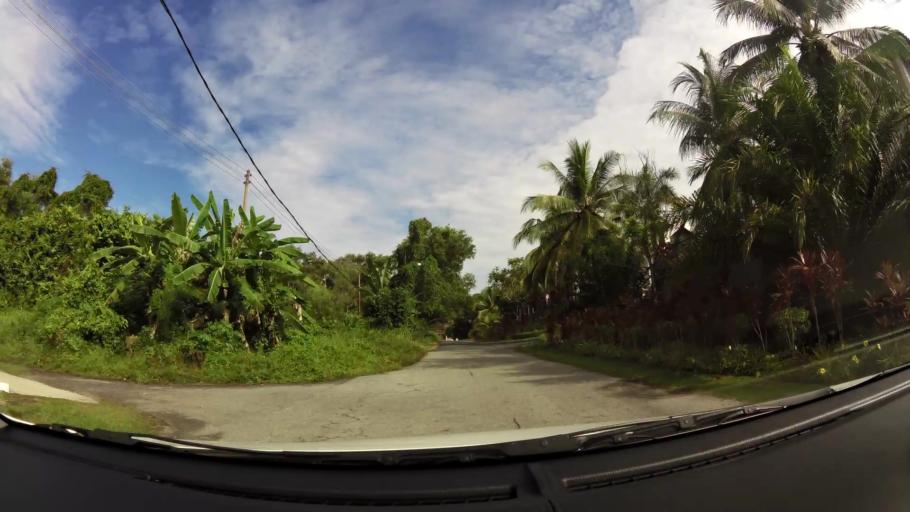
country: BN
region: Brunei and Muara
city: Bandar Seri Begawan
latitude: 4.9176
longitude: 114.8982
